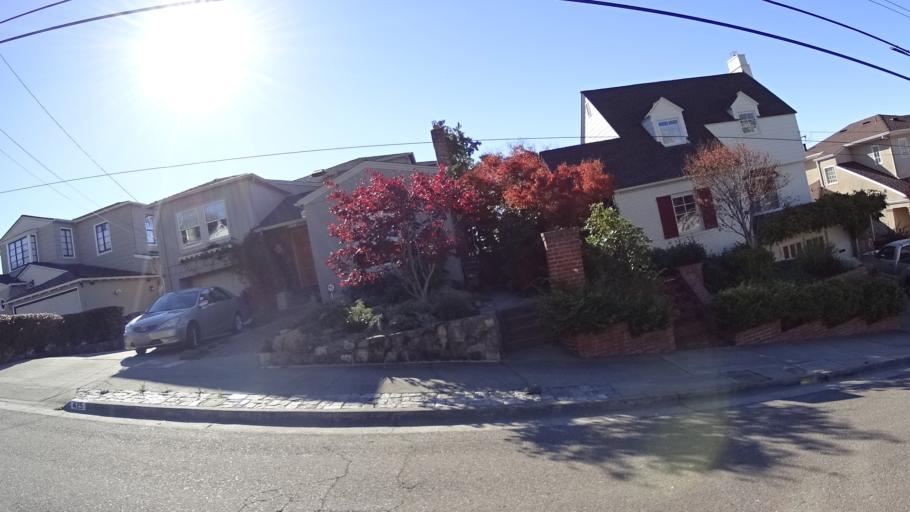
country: US
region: California
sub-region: Alameda County
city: Piedmont
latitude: 37.8385
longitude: -122.2273
